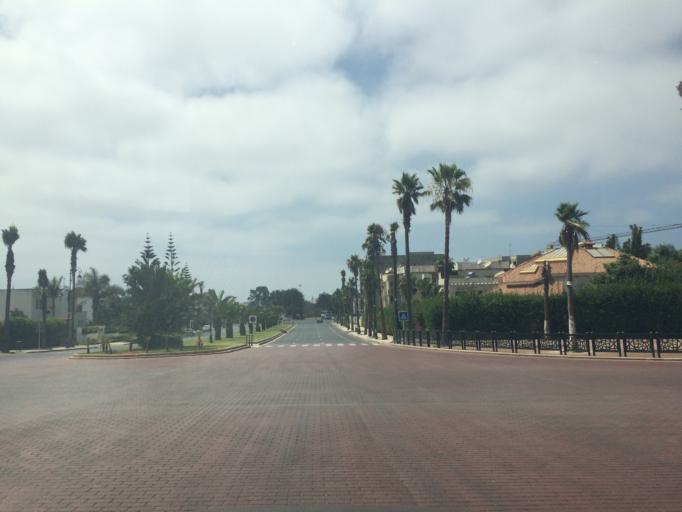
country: MA
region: Rabat-Sale-Zemmour-Zaer
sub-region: Skhirate-Temara
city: Temara
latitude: 33.9630
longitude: -6.8797
